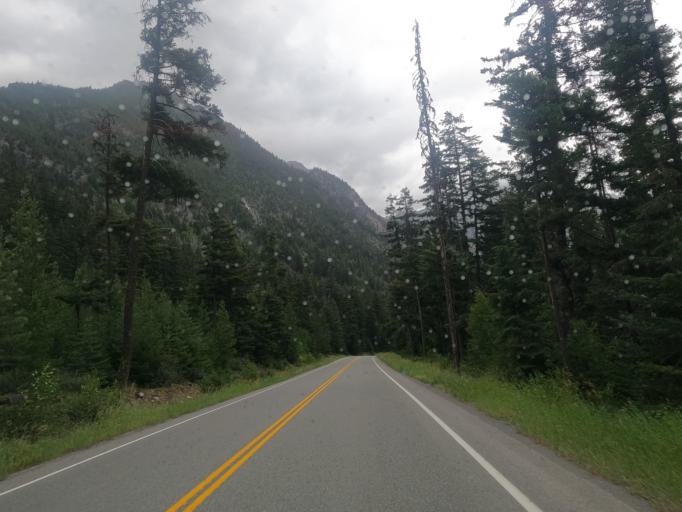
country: CA
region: British Columbia
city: Lillooet
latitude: 50.5091
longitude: -122.1728
